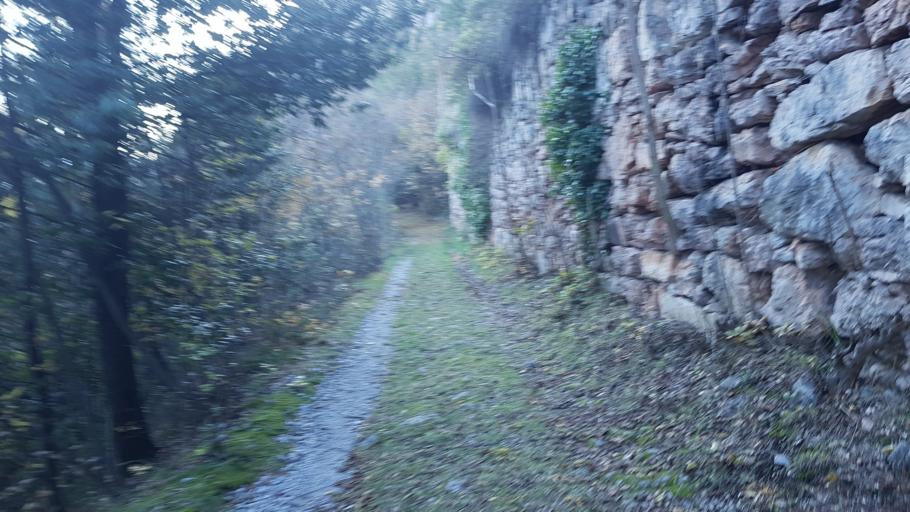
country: IT
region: Trentino-Alto Adige
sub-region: Provincia di Trento
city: Vezzano
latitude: 46.0768
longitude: 10.9821
